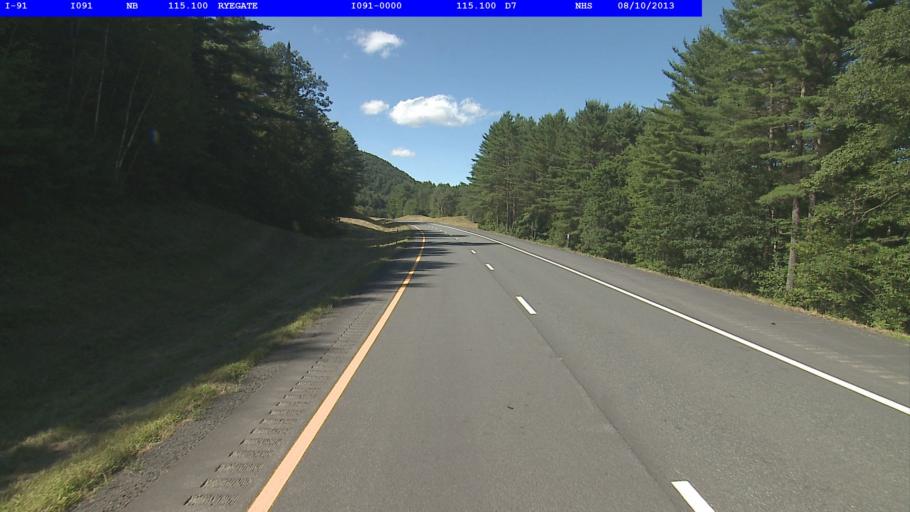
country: US
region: New Hampshire
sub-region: Grafton County
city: Woodsville
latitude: 44.2263
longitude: -72.0670
